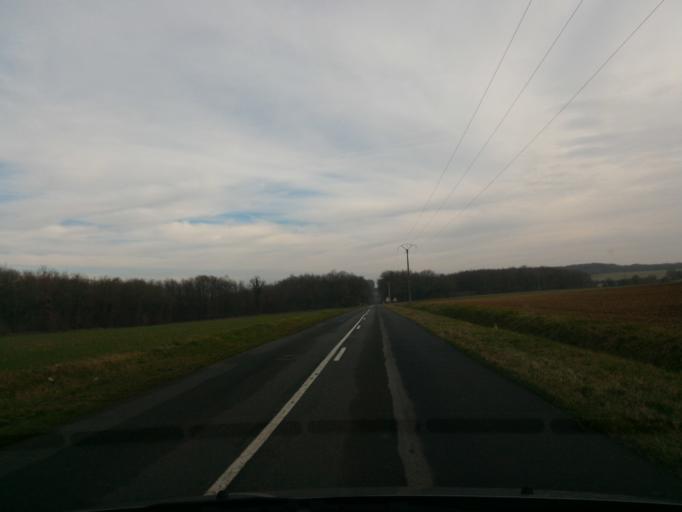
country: FR
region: Poitou-Charentes
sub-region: Departement de la Charente
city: Aigre
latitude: 45.9180
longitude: 0.0472
